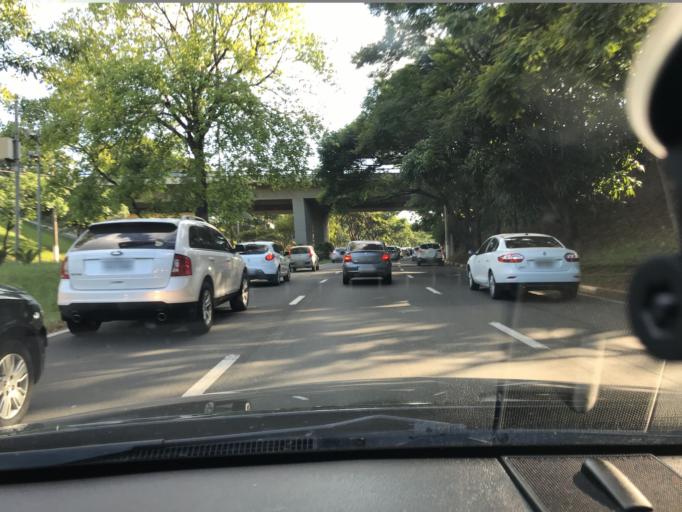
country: BR
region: Sao Paulo
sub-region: Campinas
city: Campinas
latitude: -22.9149
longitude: -47.0593
